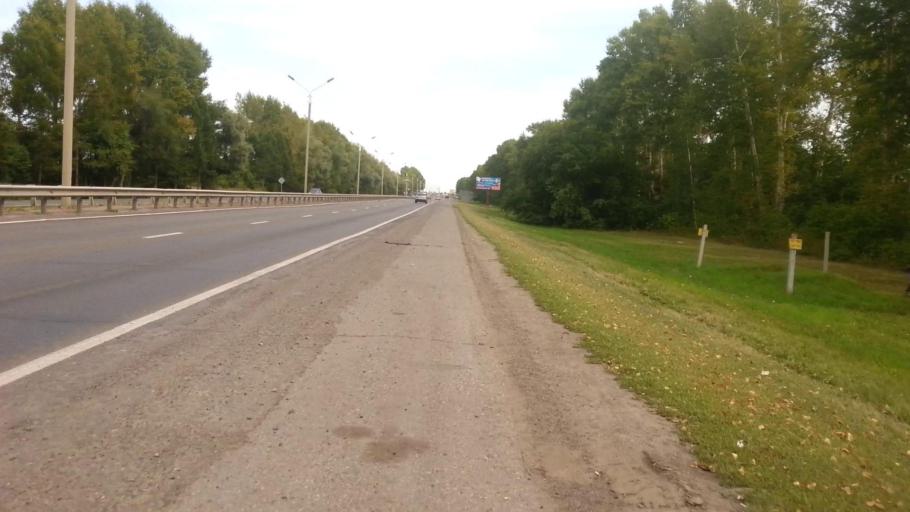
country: RU
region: Altai Krai
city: Vlasikha
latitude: 53.3524
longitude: 83.5713
